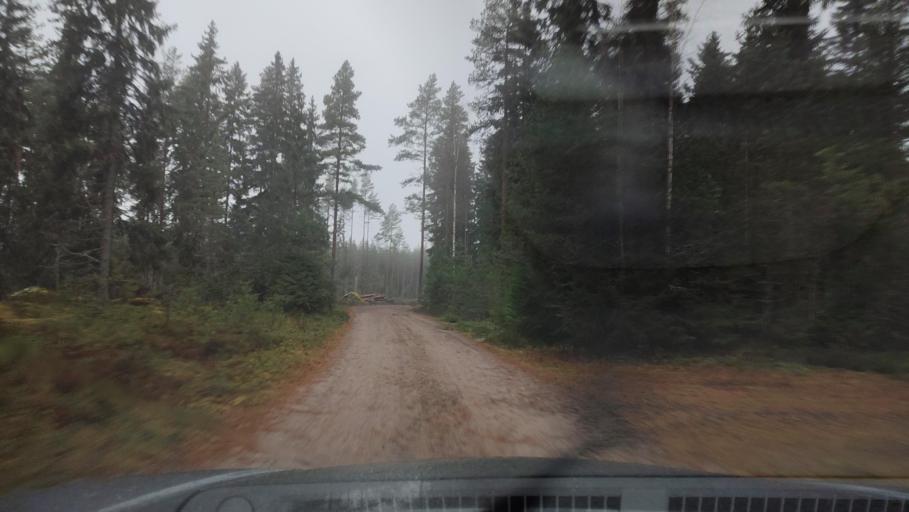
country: FI
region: Southern Ostrobothnia
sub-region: Suupohja
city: Karijoki
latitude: 62.1972
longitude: 21.7826
